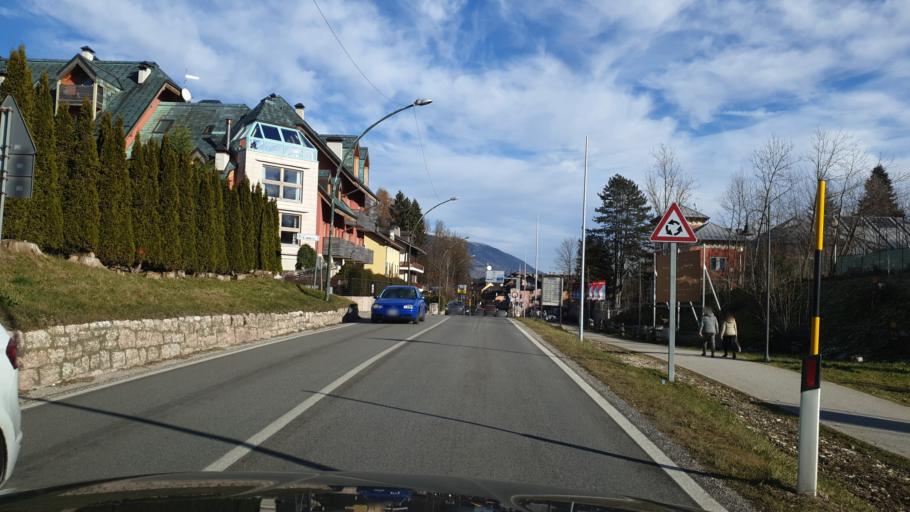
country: IT
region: Veneto
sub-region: Provincia di Vicenza
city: Asiago
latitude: 45.8730
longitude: 11.5035
